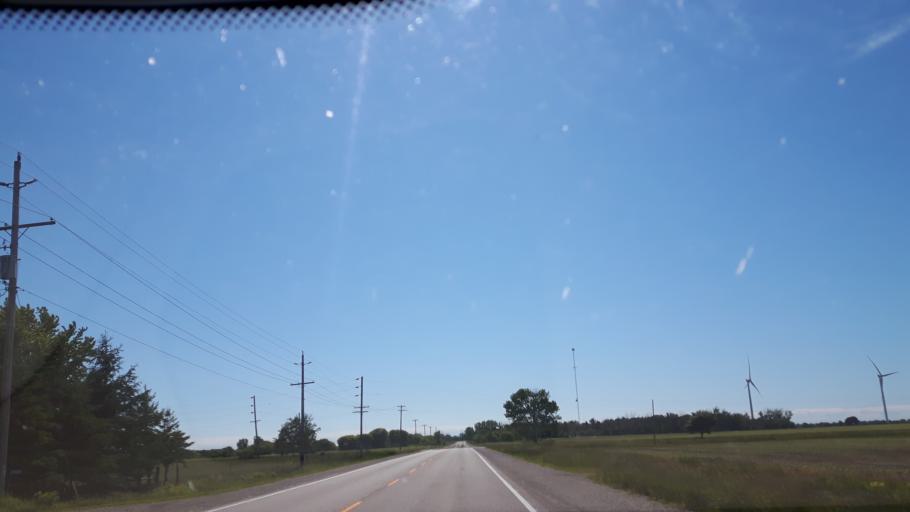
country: CA
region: Ontario
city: Bluewater
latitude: 43.4161
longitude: -81.6732
